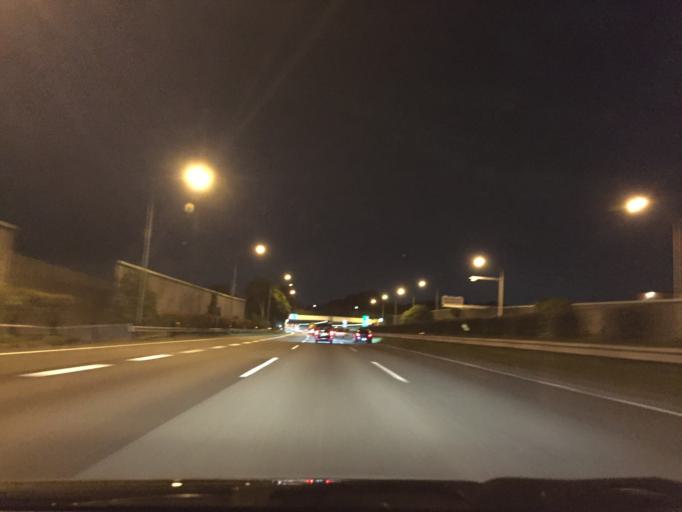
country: JP
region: Kanagawa
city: Minami-rinkan
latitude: 35.4785
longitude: 139.4530
